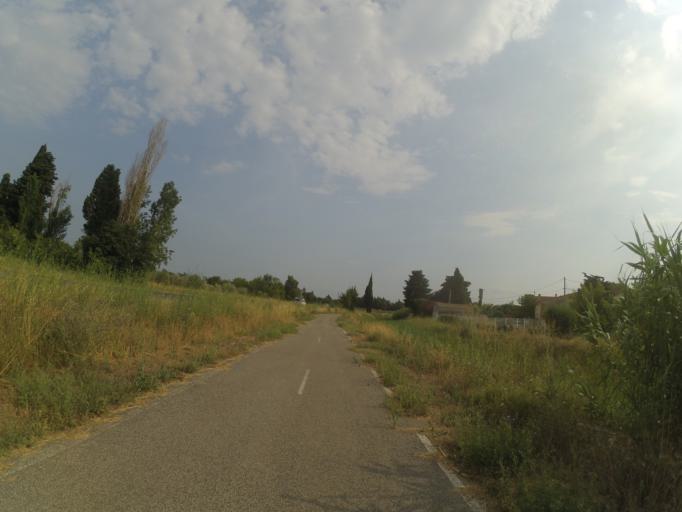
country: FR
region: Languedoc-Roussillon
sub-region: Departement des Pyrenees-Orientales
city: Pezilla-la-Riviere
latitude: 42.6909
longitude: 2.7520
